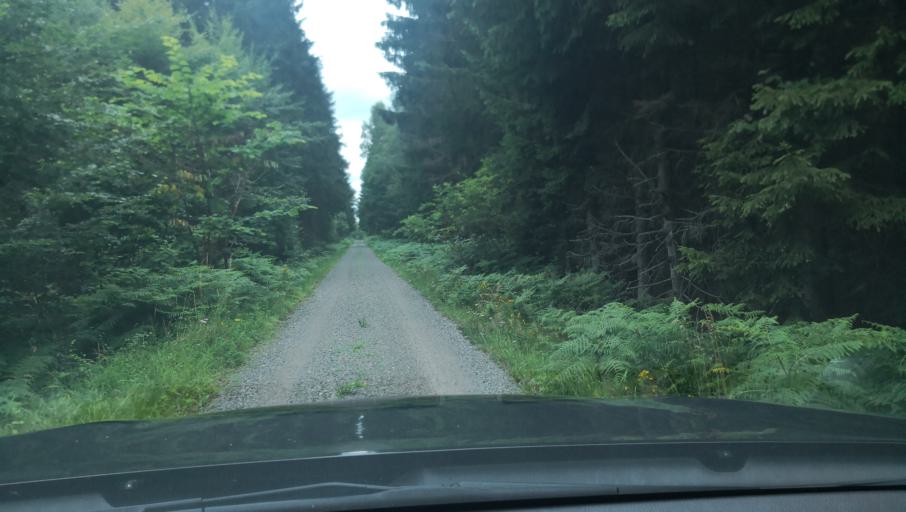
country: SE
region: Skane
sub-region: Simrishamns Kommun
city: Kivik
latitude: 55.6106
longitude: 14.1144
